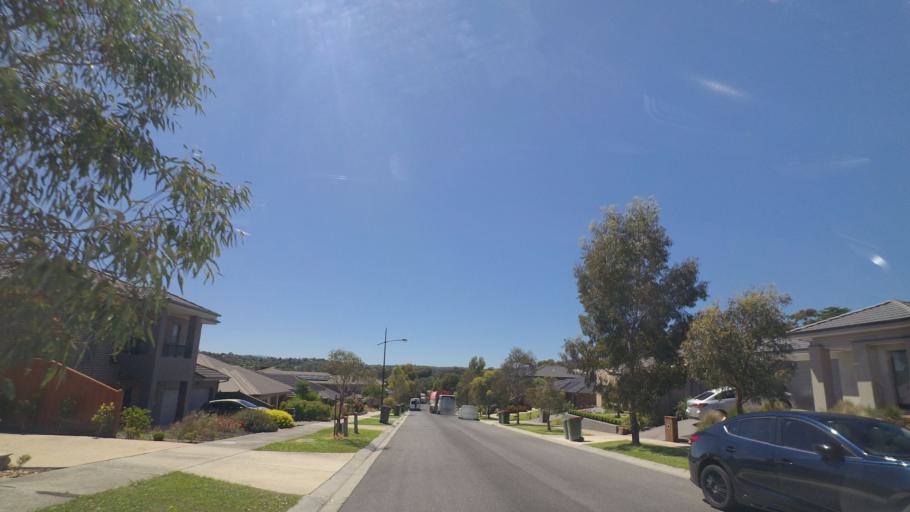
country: AU
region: Victoria
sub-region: Maroondah
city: Croydon North
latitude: -37.7811
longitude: 145.2972
